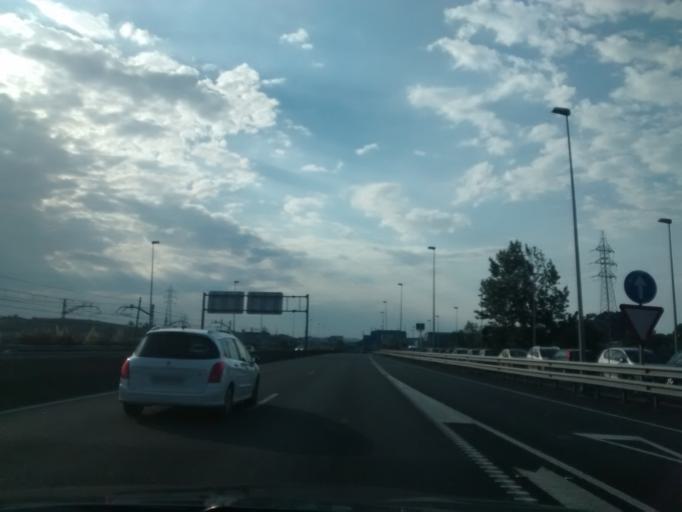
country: ES
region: Cantabria
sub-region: Provincia de Cantabria
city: El Astillero
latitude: 43.4065
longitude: -3.8260
